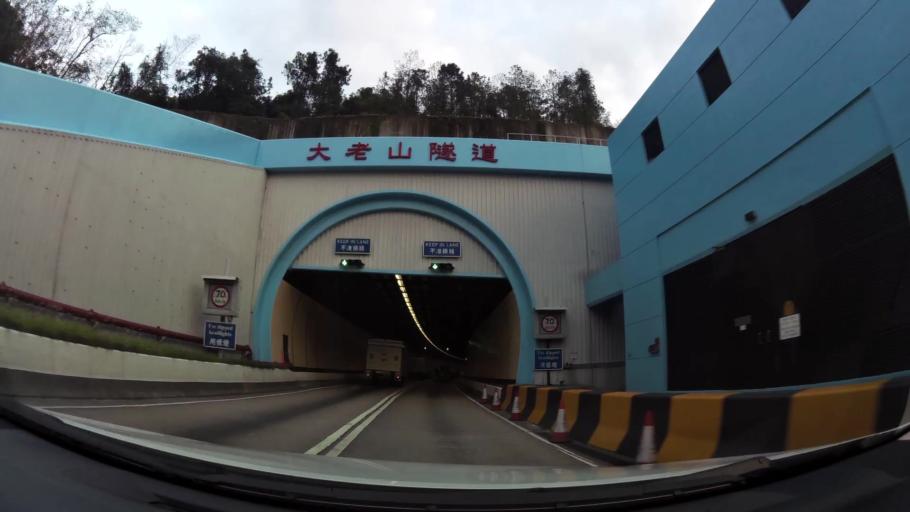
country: HK
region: Sha Tin
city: Sha Tin
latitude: 22.3766
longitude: 114.2141
